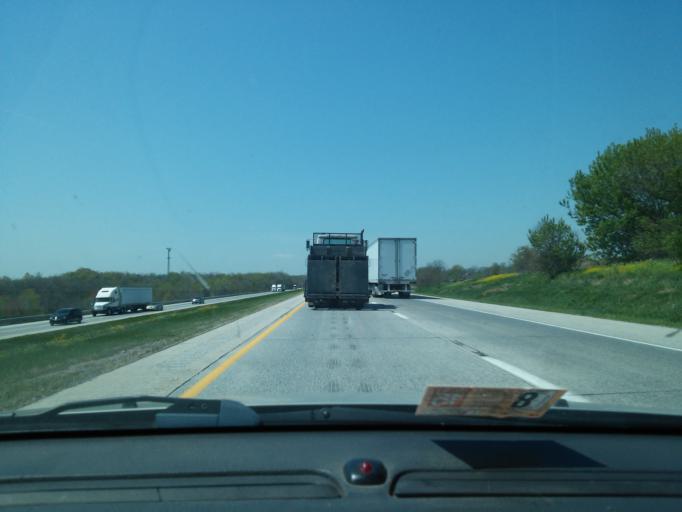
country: US
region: Pennsylvania
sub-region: Lebanon County
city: Jonestown
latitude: 40.4452
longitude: -76.4697
